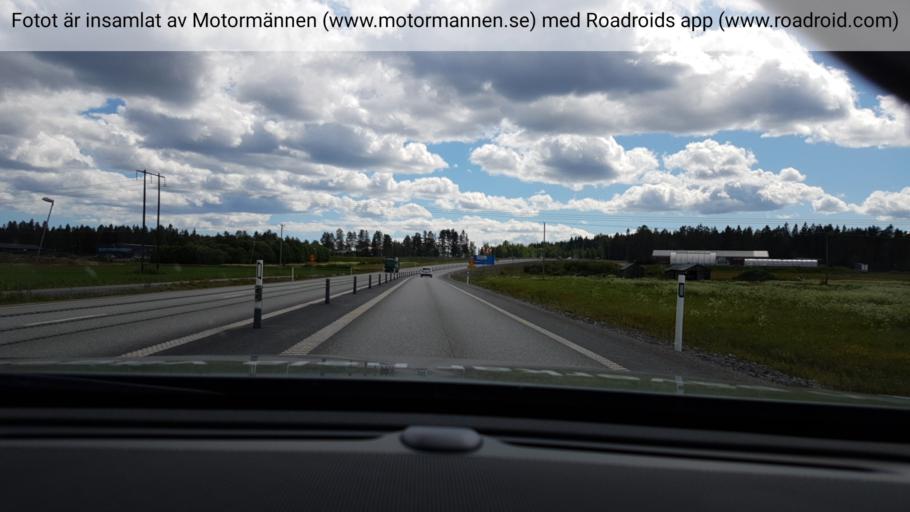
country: SE
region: Vaesterbotten
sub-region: Umea Kommun
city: Roback
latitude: 63.8459
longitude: 20.1905
